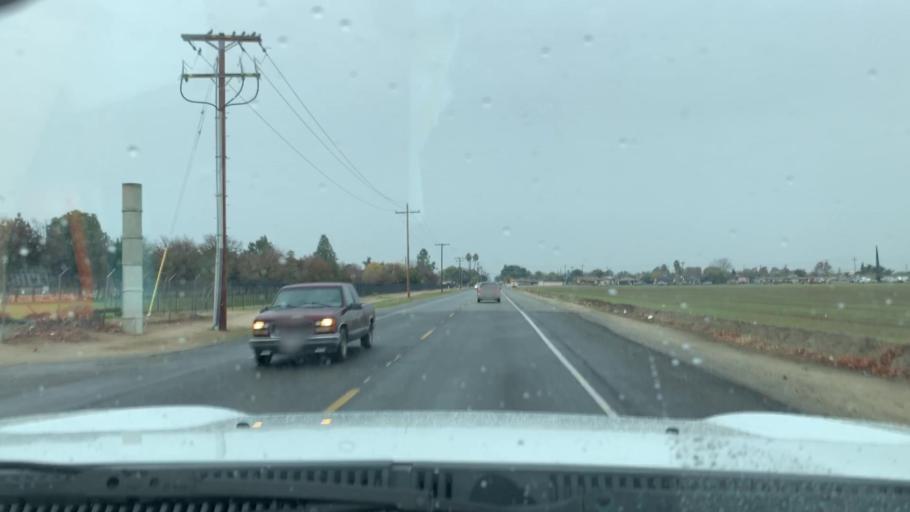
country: US
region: California
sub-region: Kern County
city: Delano
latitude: 35.7614
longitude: -119.2628
